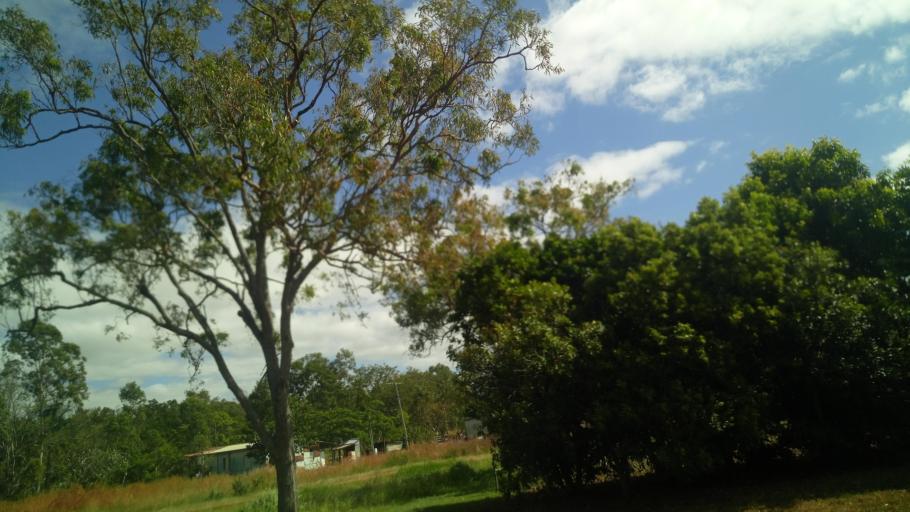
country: AU
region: Queensland
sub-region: Tablelands
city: Mareeba
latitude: -16.9753
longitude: 145.4571
